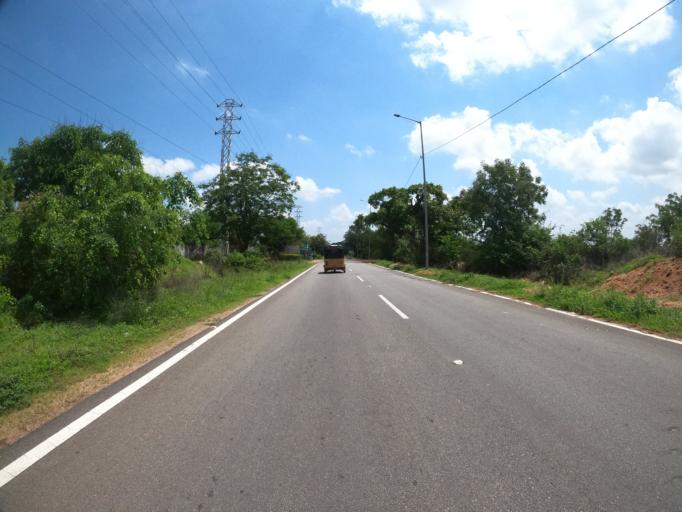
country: IN
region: Telangana
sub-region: Rangareddi
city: Sriramnagar
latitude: 17.3595
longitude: 78.3228
